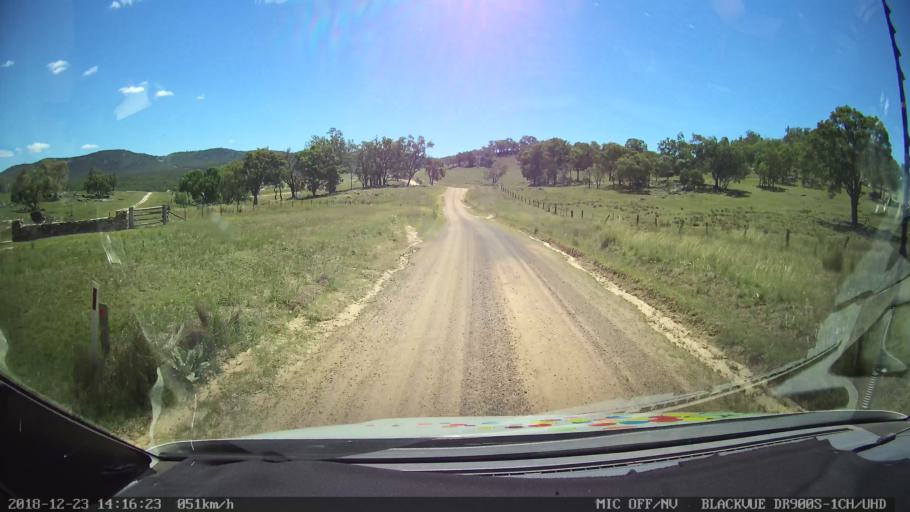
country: AU
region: New South Wales
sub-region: Tamworth Municipality
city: Manilla
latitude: -30.6605
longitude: 151.0182
